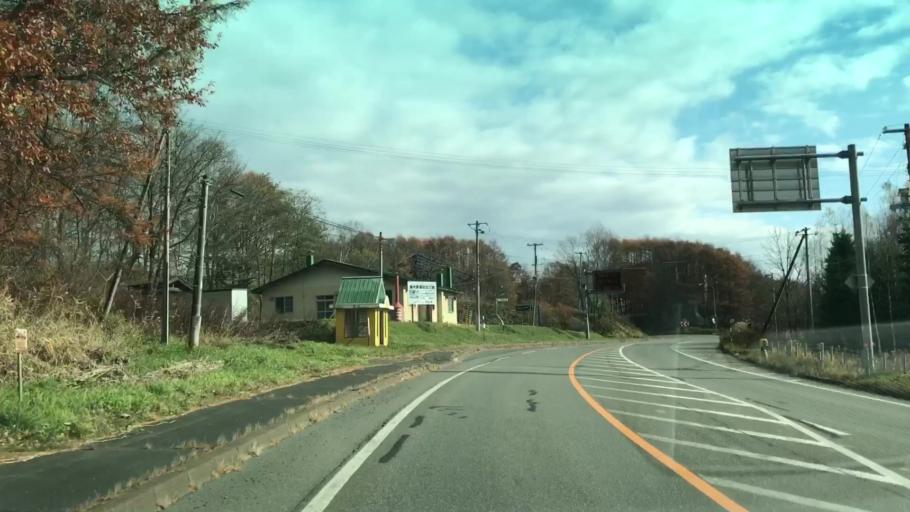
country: JP
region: Hokkaido
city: Shizunai-furukawacho
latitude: 42.7180
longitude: 142.2615
